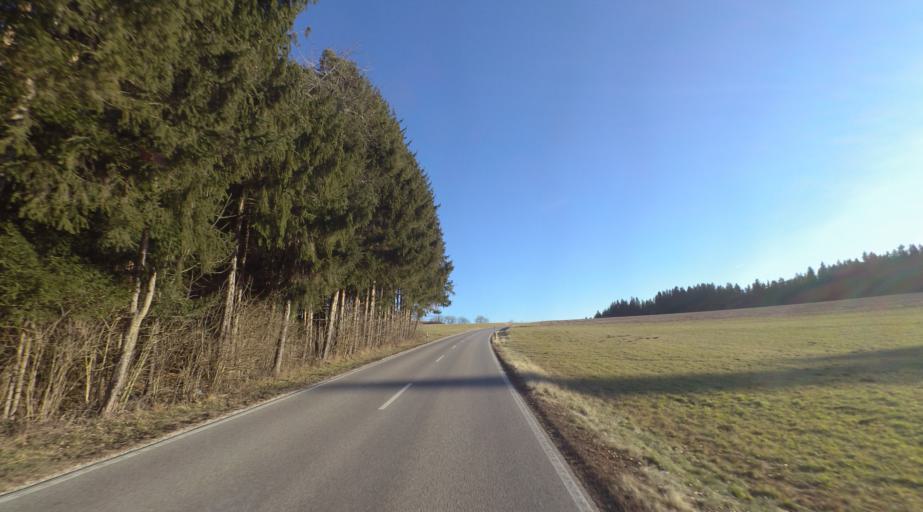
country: DE
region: Bavaria
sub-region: Upper Bavaria
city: Palling
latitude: 48.0116
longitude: 12.6180
